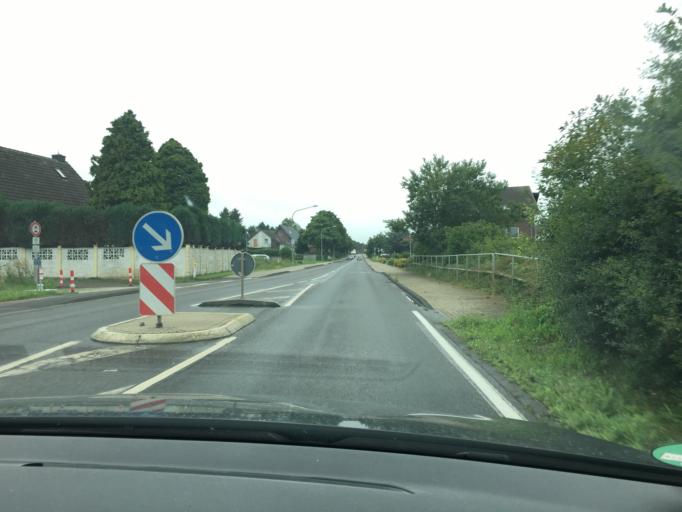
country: DE
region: North Rhine-Westphalia
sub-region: Regierungsbezirk Koln
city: Hurtgenwald
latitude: 50.7160
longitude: 6.3865
